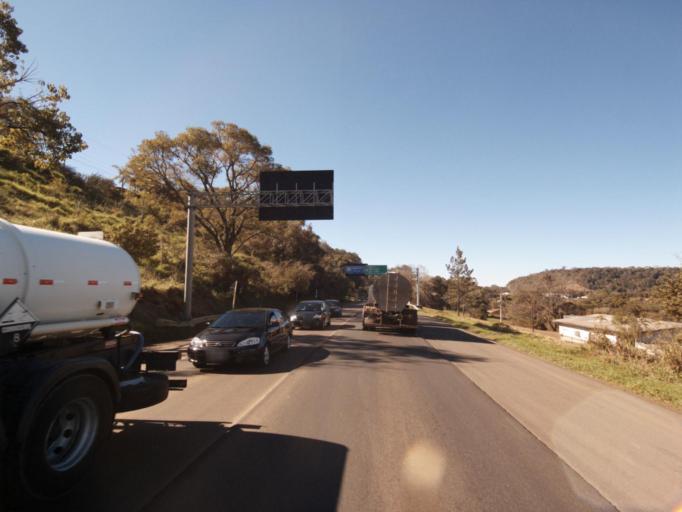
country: BR
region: Santa Catarina
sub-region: Chapeco
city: Chapeco
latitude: -26.9980
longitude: -52.6433
